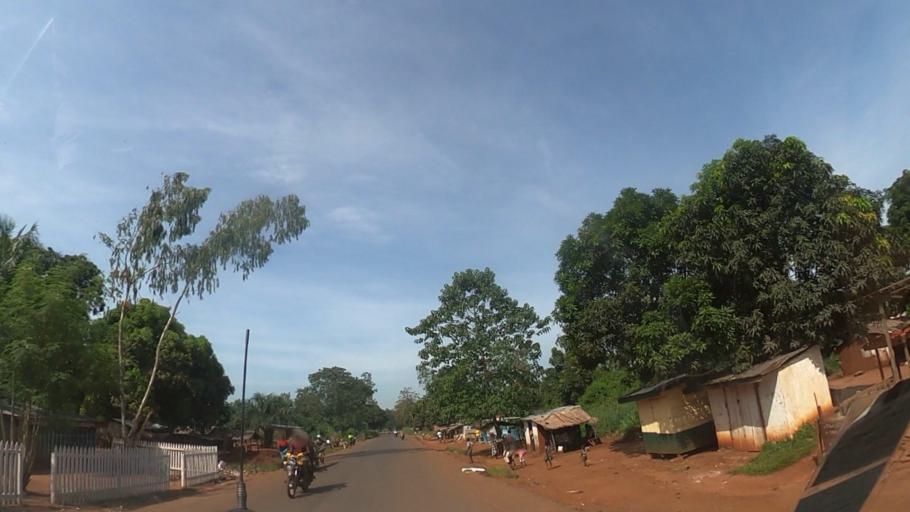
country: CF
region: Bangui
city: Bangui
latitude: 4.3126
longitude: 18.4865
